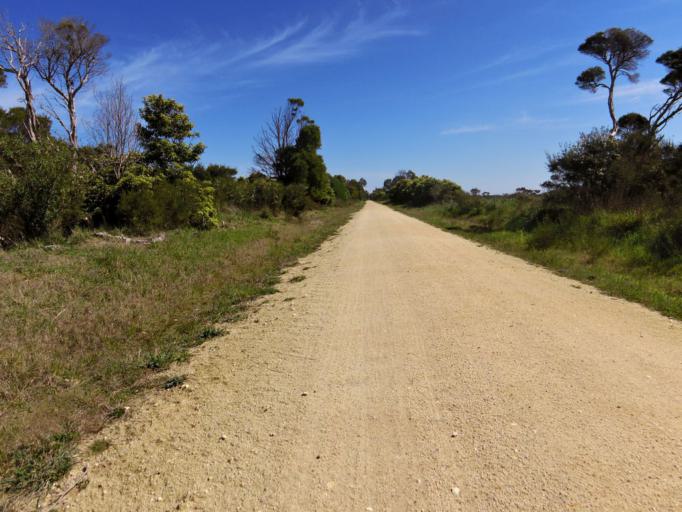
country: AU
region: Victoria
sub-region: Latrobe
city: Morwell
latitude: -38.6701
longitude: 146.4174
